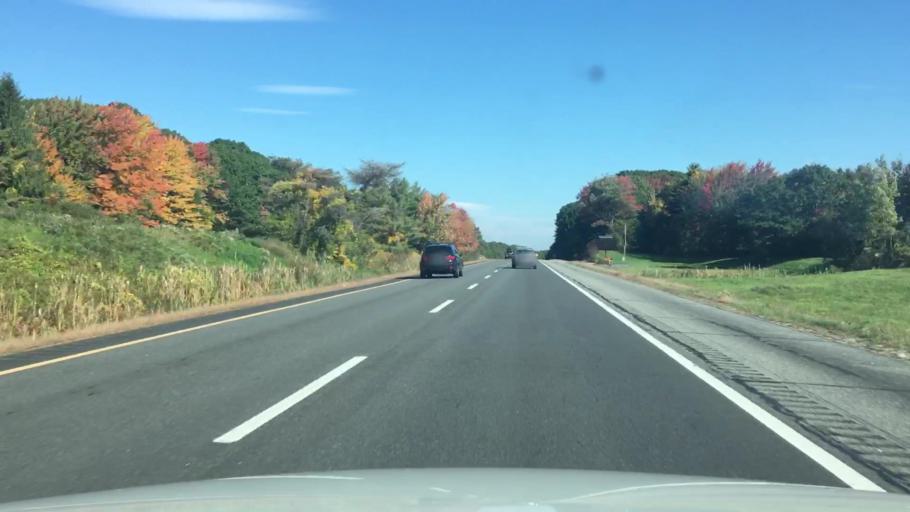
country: US
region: Maine
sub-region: Cumberland County
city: Falmouth
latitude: 43.7029
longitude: -70.2557
